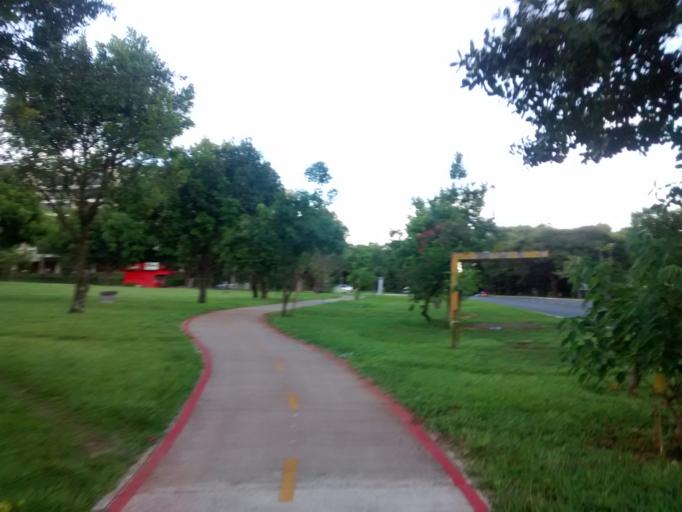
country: BR
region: Federal District
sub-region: Brasilia
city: Brasilia
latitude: -15.7722
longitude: -47.8781
